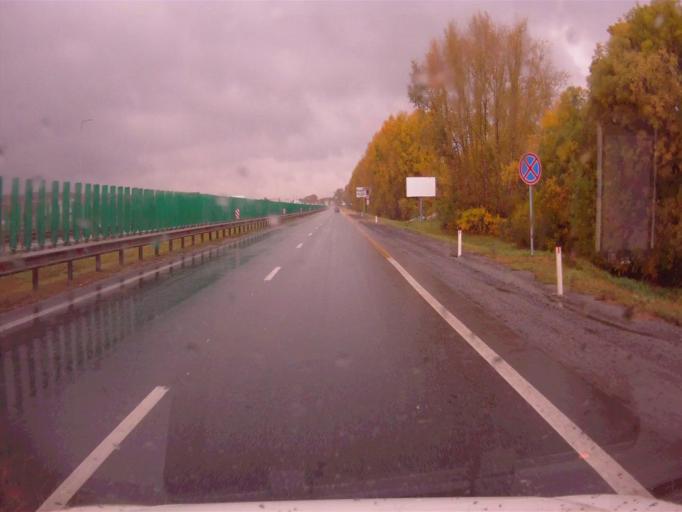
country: RU
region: Chelyabinsk
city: Dolgoderevenskoye
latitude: 55.2783
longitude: 61.3436
